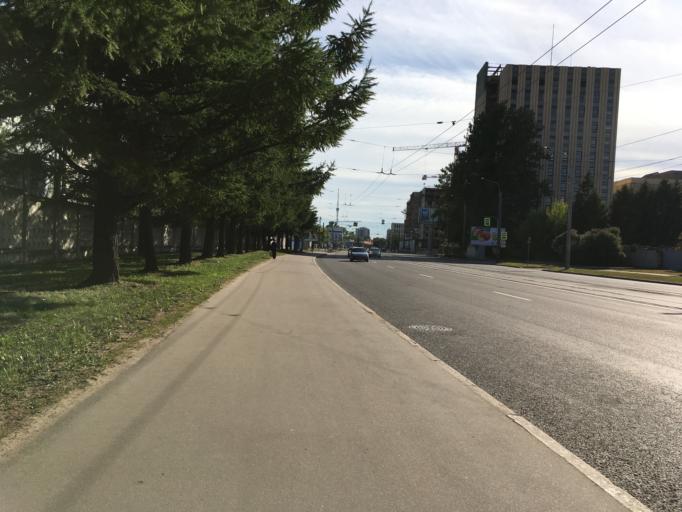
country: RU
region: St.-Petersburg
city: Kushelevka
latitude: 59.9949
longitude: 30.3618
